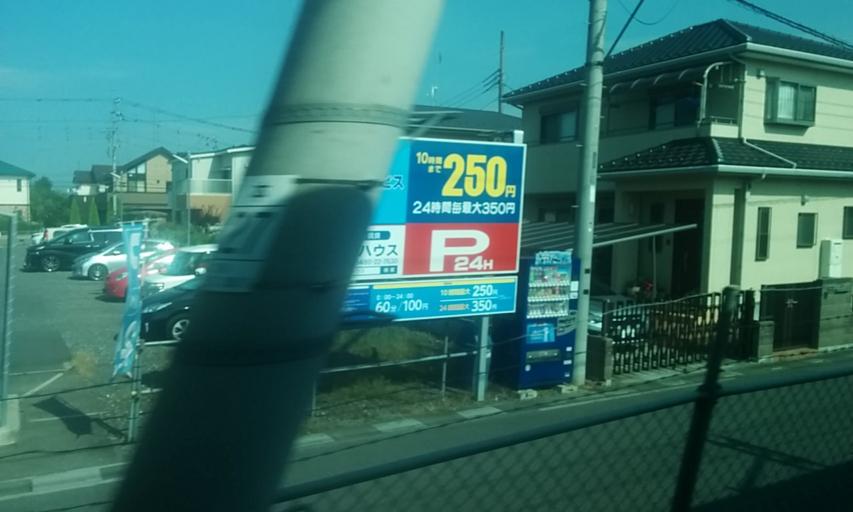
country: JP
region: Saitama
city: Shiraoka
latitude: 36.0362
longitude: 139.6716
